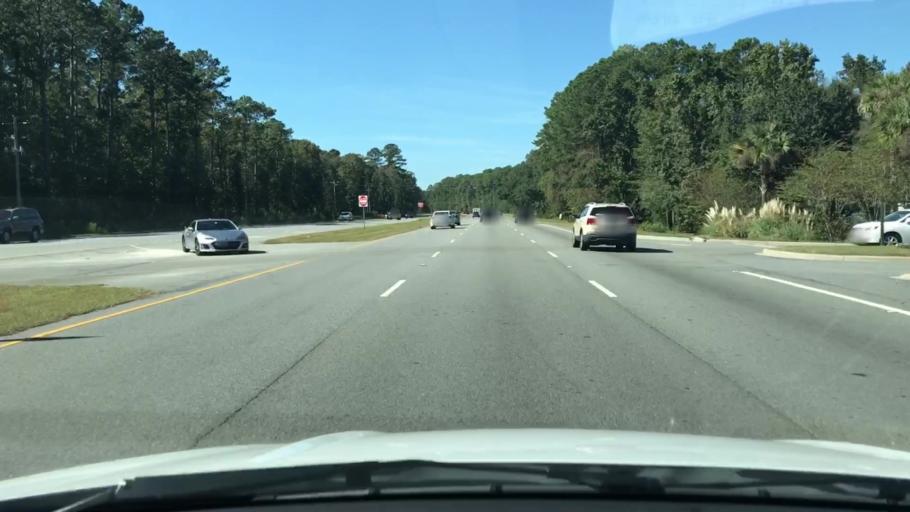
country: US
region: South Carolina
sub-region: Beaufort County
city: Bluffton
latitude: 32.2880
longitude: -80.8939
